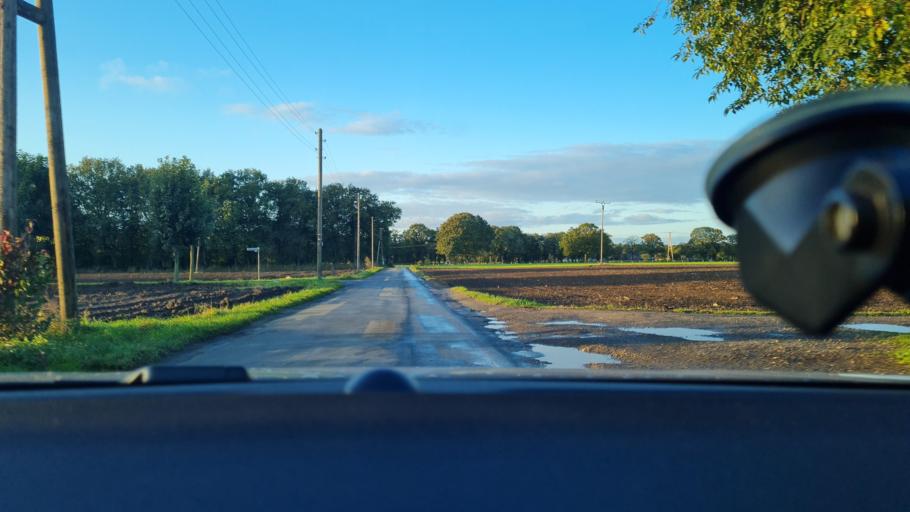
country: DE
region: North Rhine-Westphalia
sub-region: Regierungsbezirk Dusseldorf
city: Dinslaken
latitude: 51.5963
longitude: 6.7343
